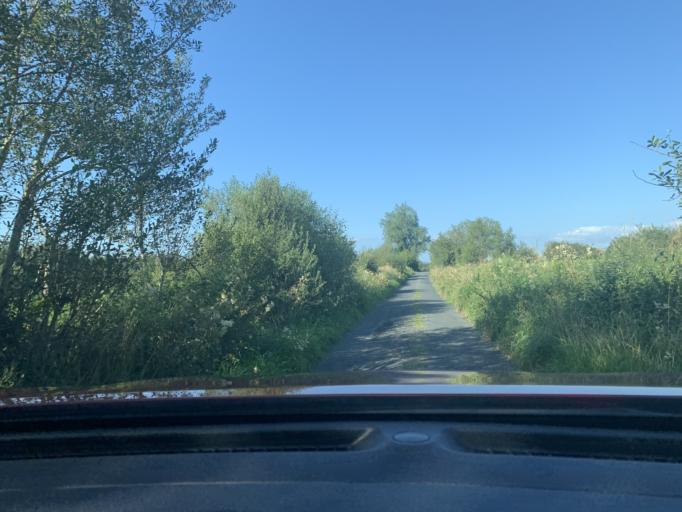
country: IE
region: Connaught
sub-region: Sligo
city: Tobercurry
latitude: 54.0650
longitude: -8.7812
